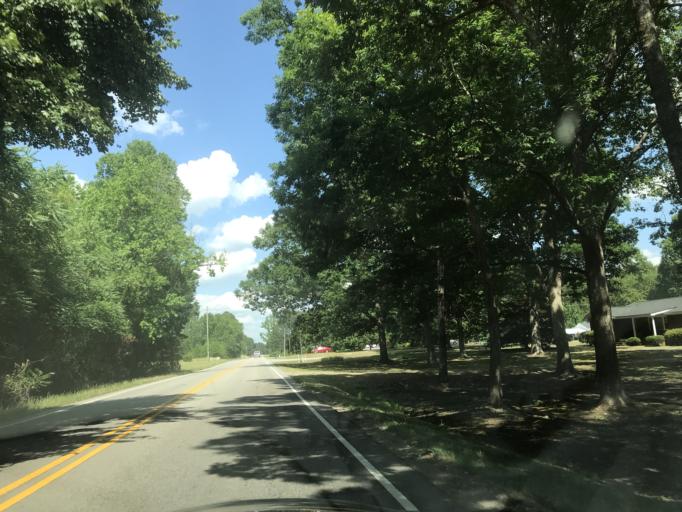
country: US
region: North Carolina
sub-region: Wake County
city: Rolesville
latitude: 35.9730
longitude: -78.3775
